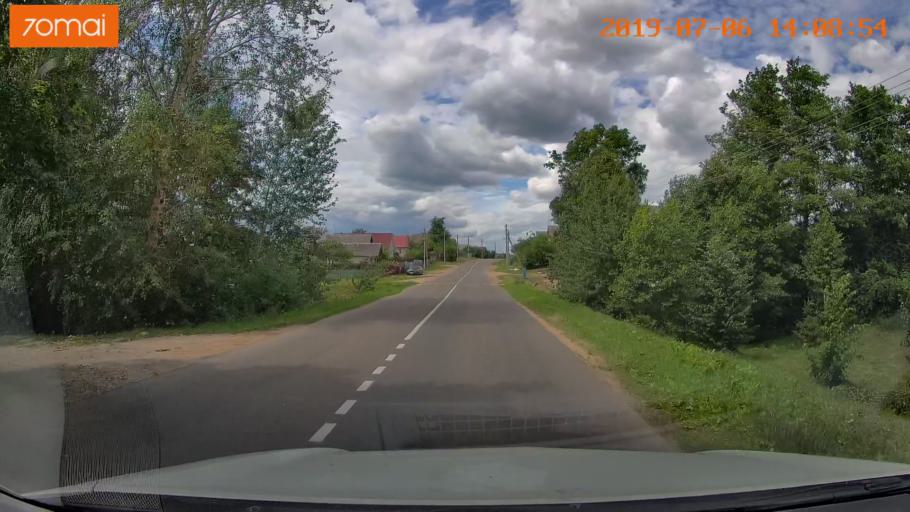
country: BY
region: Minsk
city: Ivyanyets
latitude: 53.8783
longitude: 26.7525
